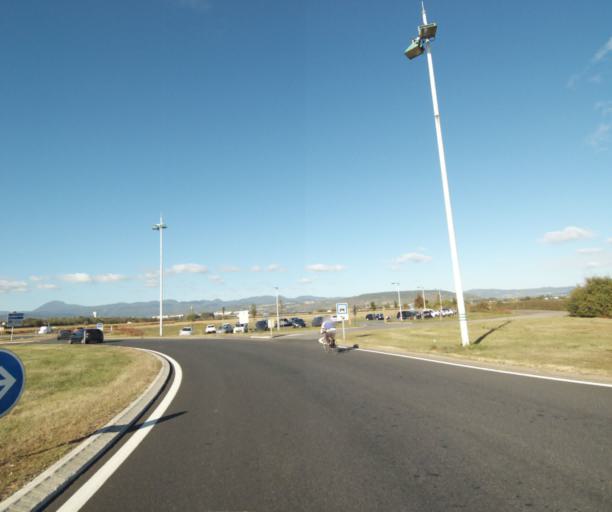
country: FR
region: Auvergne
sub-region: Departement du Puy-de-Dome
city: Gerzat
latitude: 45.8467
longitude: 3.1666
